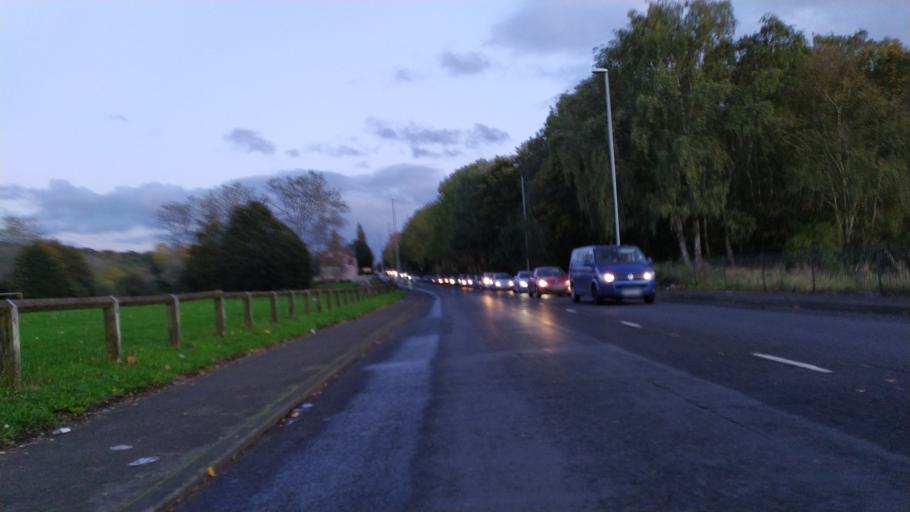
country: GB
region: England
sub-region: City and Borough of Leeds
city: Chapel Allerton
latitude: 53.8215
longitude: -1.5589
